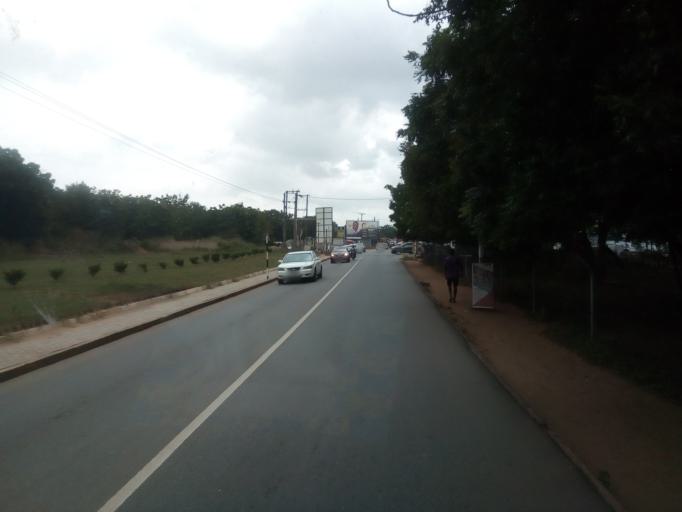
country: GH
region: Greater Accra
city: Dome
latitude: 5.6392
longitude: -0.2087
